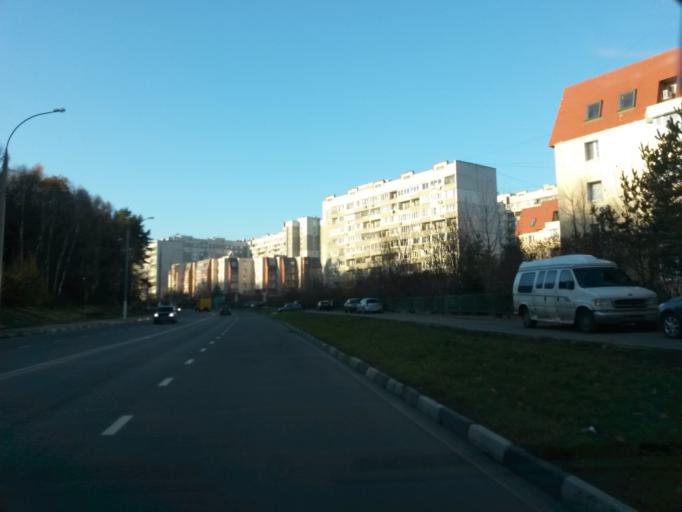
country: RU
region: Moscow
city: Annino
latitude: 55.5639
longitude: 37.5680
